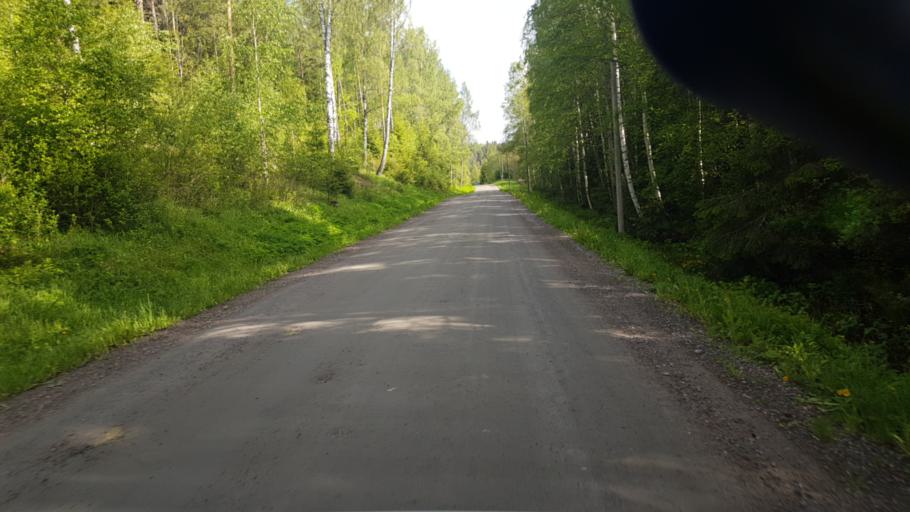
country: NO
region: Hedmark
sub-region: Eidskog
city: Skotterud
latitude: 59.8516
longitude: 11.9854
